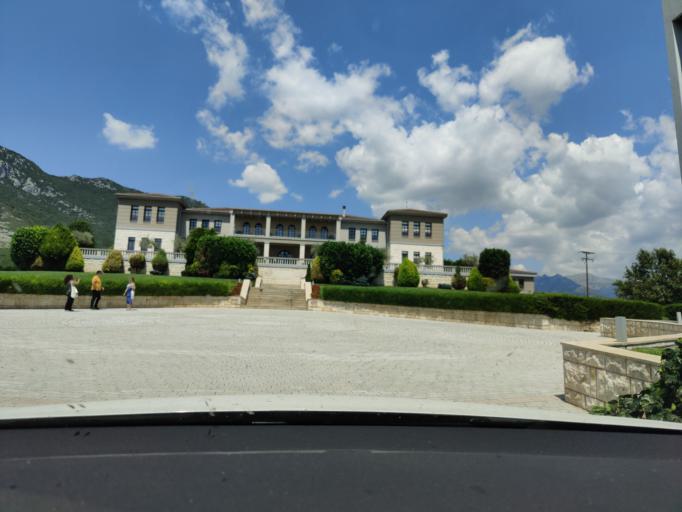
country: GR
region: East Macedonia and Thrace
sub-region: Nomos Kavalas
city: Paralia Ofryniou
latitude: 40.8112
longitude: 23.9904
